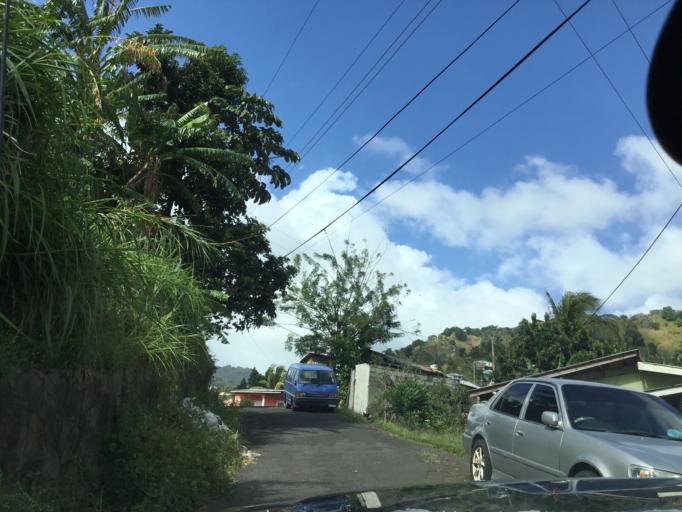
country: VC
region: Saint George
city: Kingstown
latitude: 13.1648
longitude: -61.2182
